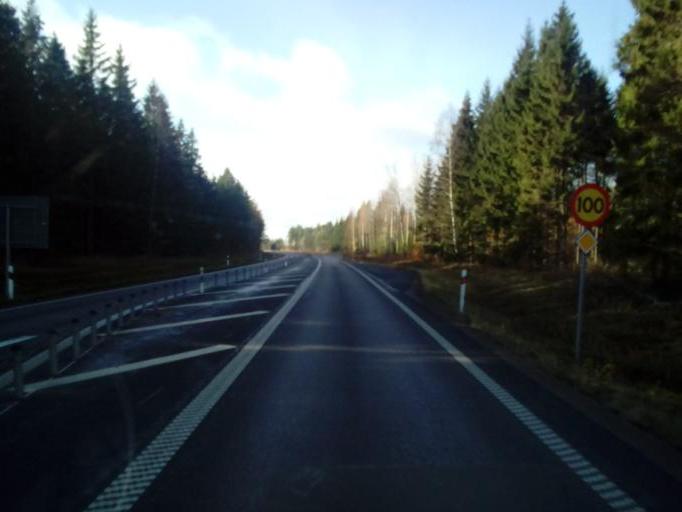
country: SE
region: Kalmar
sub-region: Vimmerby Kommun
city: Vimmerby
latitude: 57.6799
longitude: 15.9517
